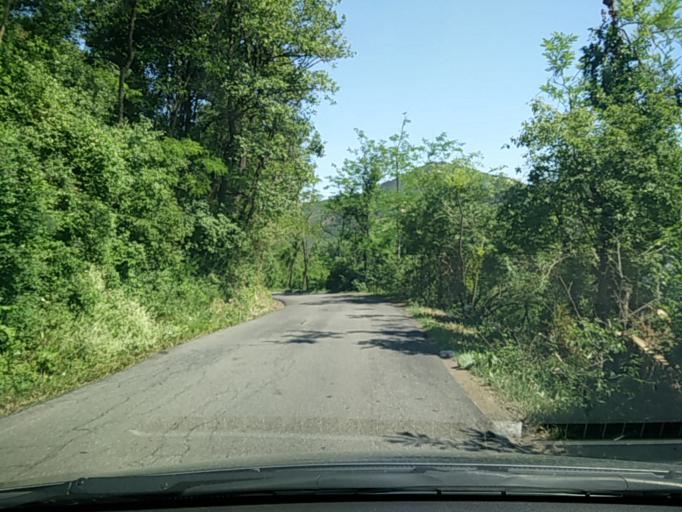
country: IT
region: Lombardy
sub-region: Provincia di Pavia
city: Godiasco
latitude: 44.9022
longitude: 9.0447
